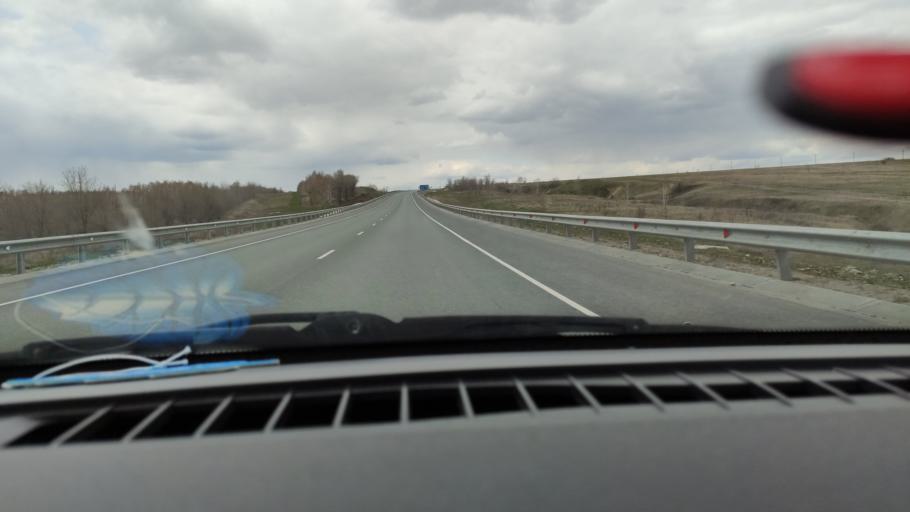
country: RU
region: Saratov
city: Shikhany
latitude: 52.1285
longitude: 47.2358
